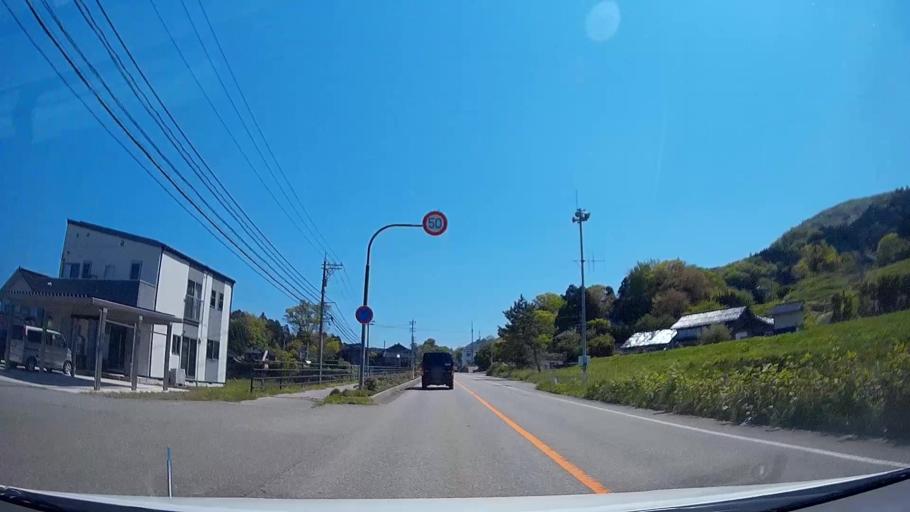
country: JP
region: Ishikawa
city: Nanao
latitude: 37.4047
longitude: 136.9555
